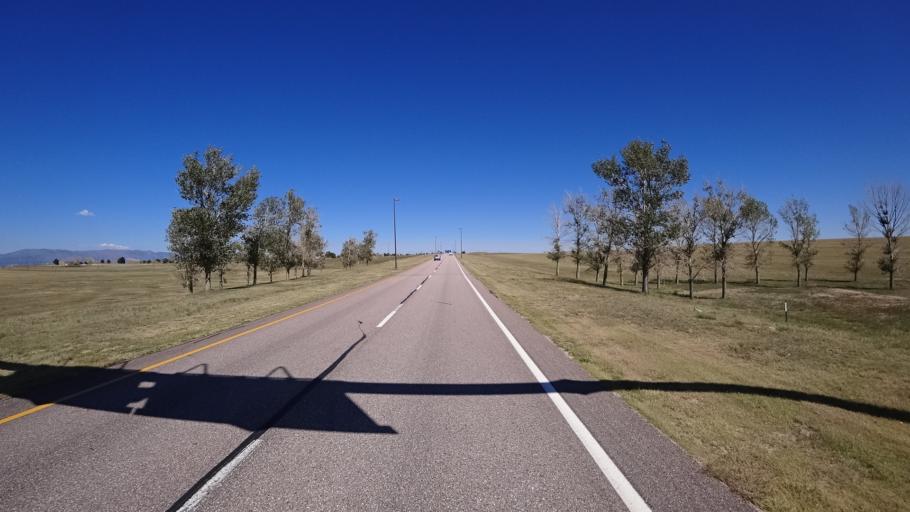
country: US
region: Colorado
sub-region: El Paso County
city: Security-Widefield
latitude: 38.7860
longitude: -104.6974
